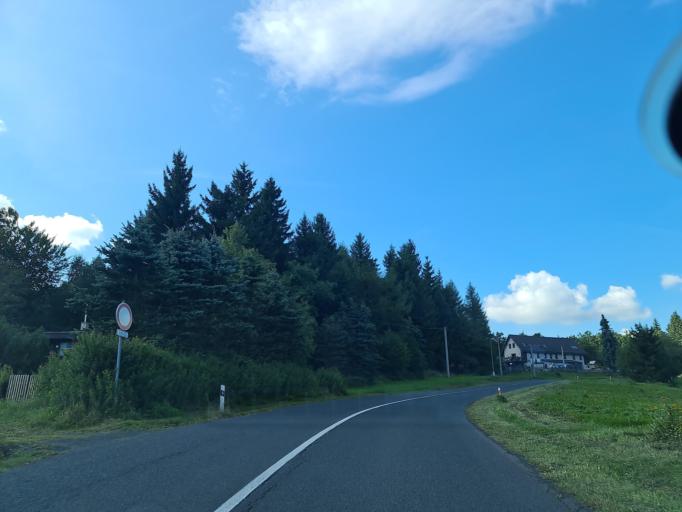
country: CZ
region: Ustecky
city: Mezibori
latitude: 50.6324
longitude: 13.5575
